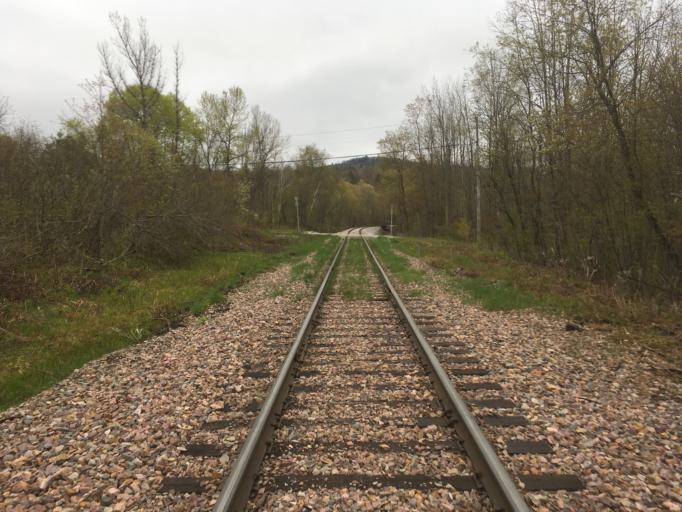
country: US
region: Vermont
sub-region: Rutland County
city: Rutland
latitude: 43.4773
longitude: -72.8735
